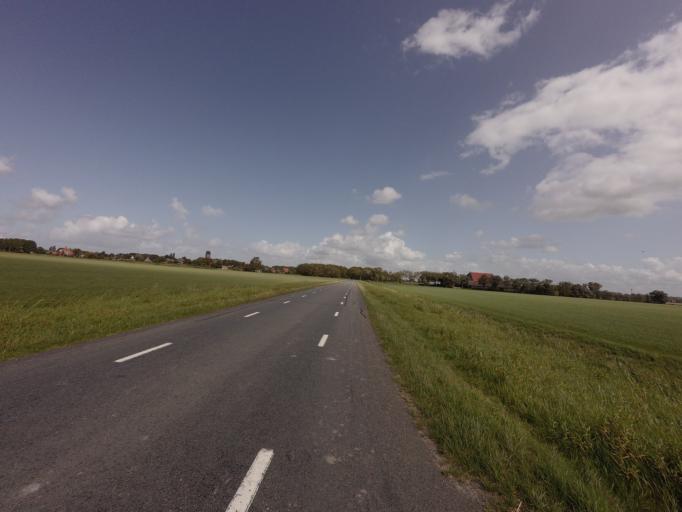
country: NL
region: Friesland
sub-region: Gemeente Harlingen
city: Harlingen
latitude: 53.1105
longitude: 5.4380
